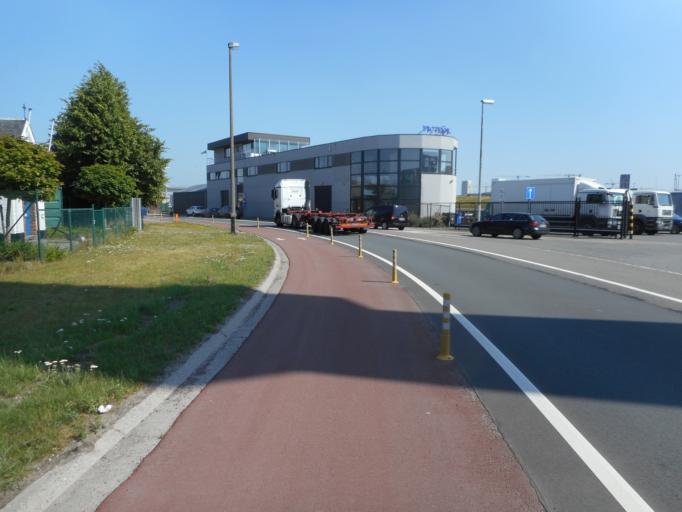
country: BE
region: Flanders
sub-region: Provincie Antwerpen
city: Antwerpen
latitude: 51.2433
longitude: 4.4088
